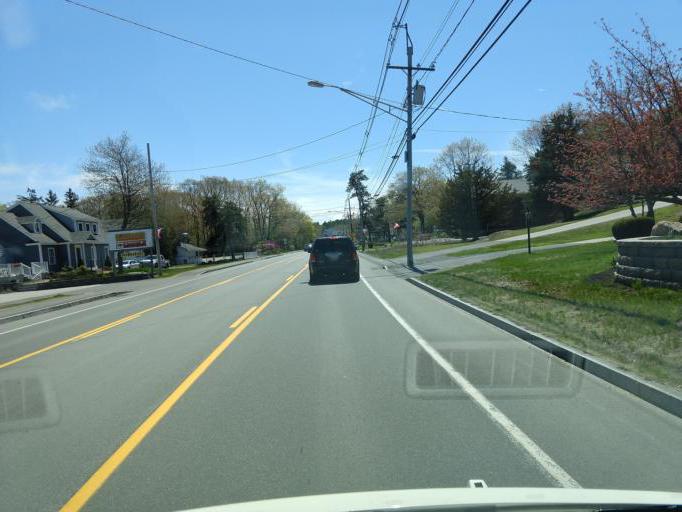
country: US
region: Maine
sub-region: York County
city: Ogunquit
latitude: 43.2564
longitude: -70.5994
